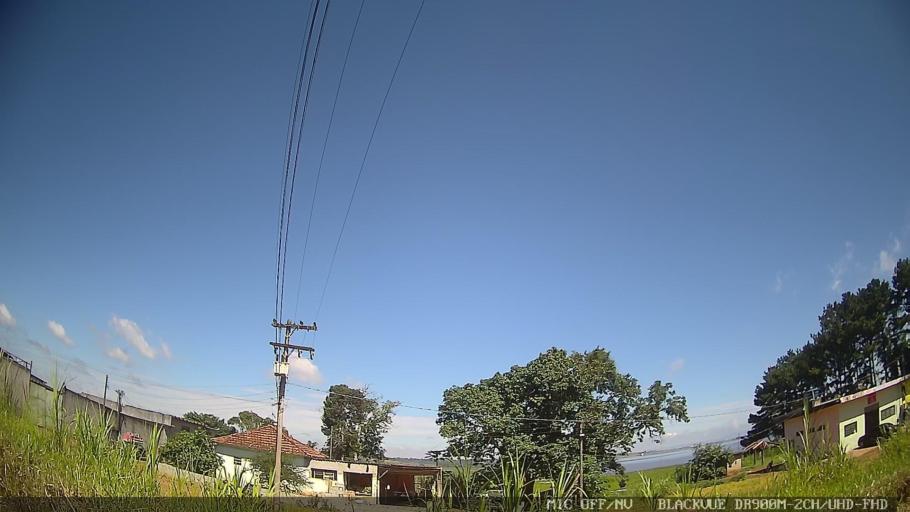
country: BR
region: Sao Paulo
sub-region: Suzano
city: Suzano
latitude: -23.6164
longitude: -46.2574
